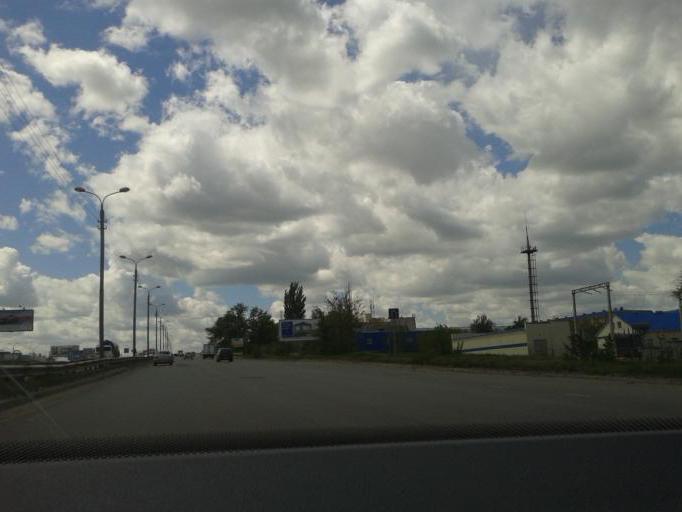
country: RU
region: Volgograd
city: Volgograd
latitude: 48.7560
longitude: 44.4886
